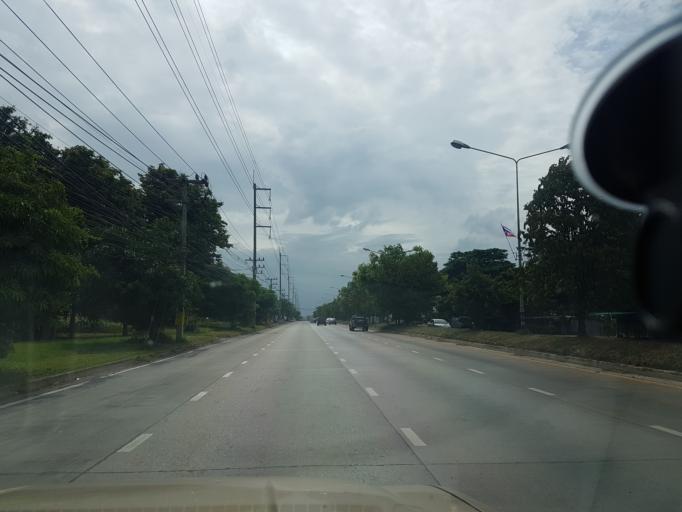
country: TH
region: Sara Buri
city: Phra Phutthabat
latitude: 14.7167
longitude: 100.8150
